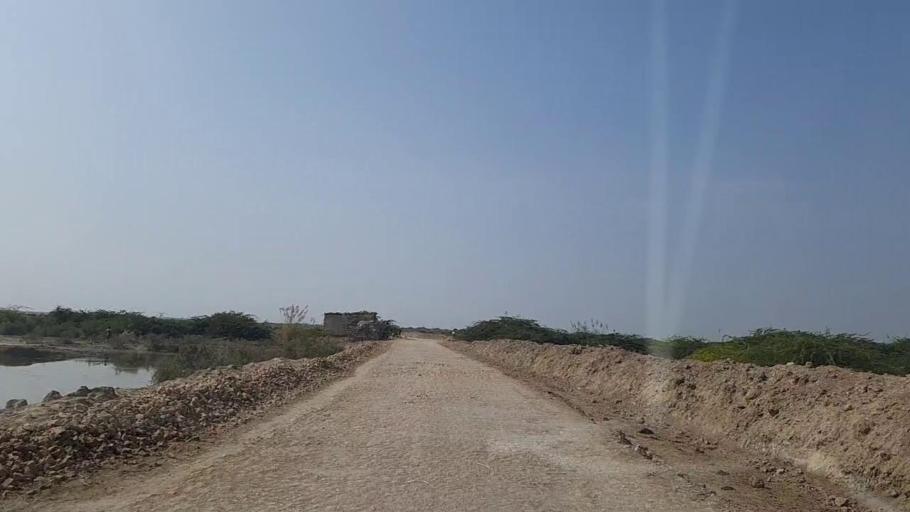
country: PK
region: Sindh
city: Chuhar Jamali
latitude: 24.1983
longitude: 67.8350
